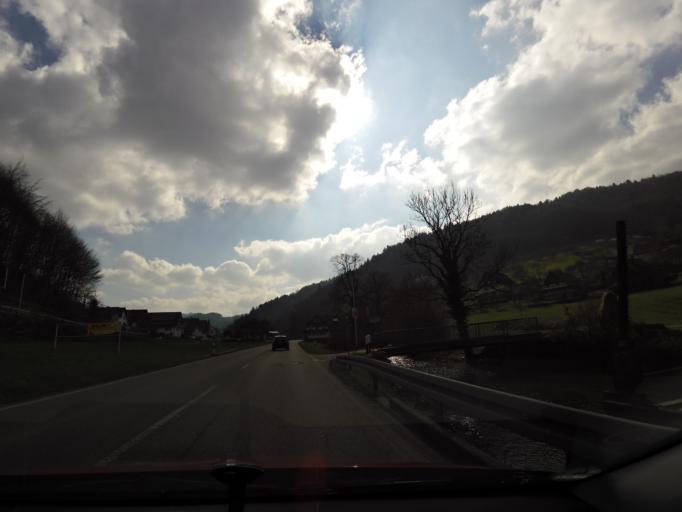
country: DE
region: Baden-Wuerttemberg
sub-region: Freiburg Region
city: Ottenhofen im Schwarzwald
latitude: 48.5786
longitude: 8.1362
